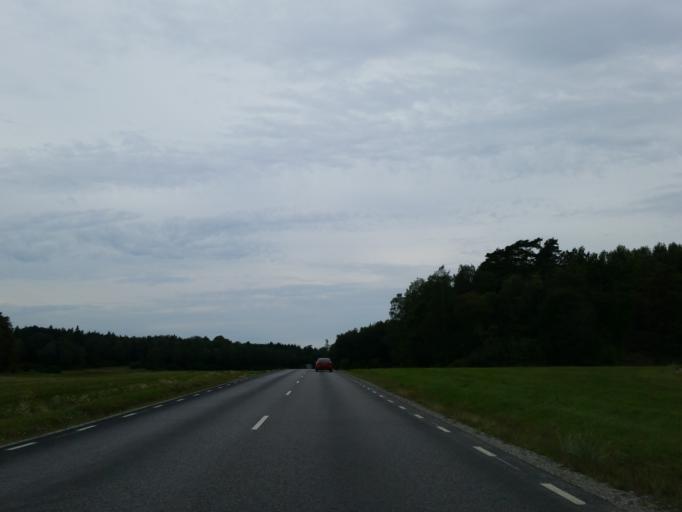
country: SE
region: Stockholm
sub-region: Salems Kommun
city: Ronninge
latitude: 59.2208
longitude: 17.7508
